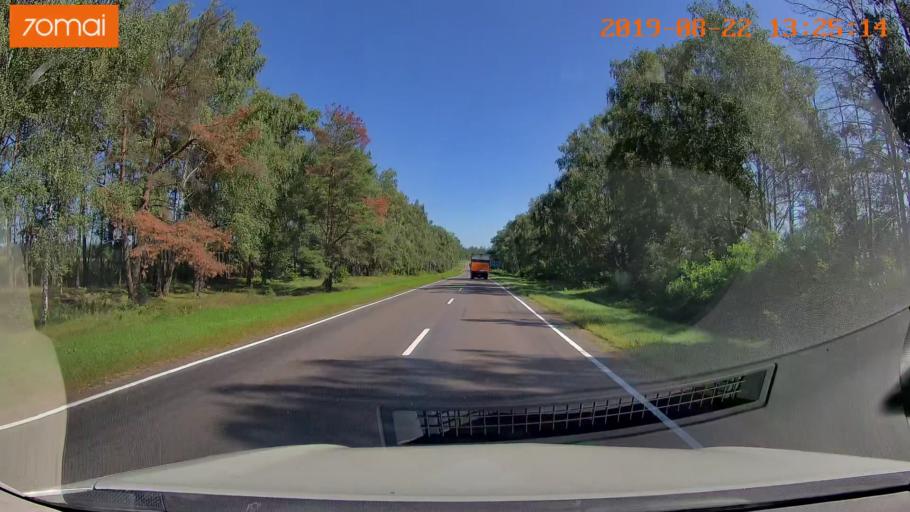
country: BY
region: Minsk
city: Staryya Darohi
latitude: 53.2117
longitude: 28.0406
